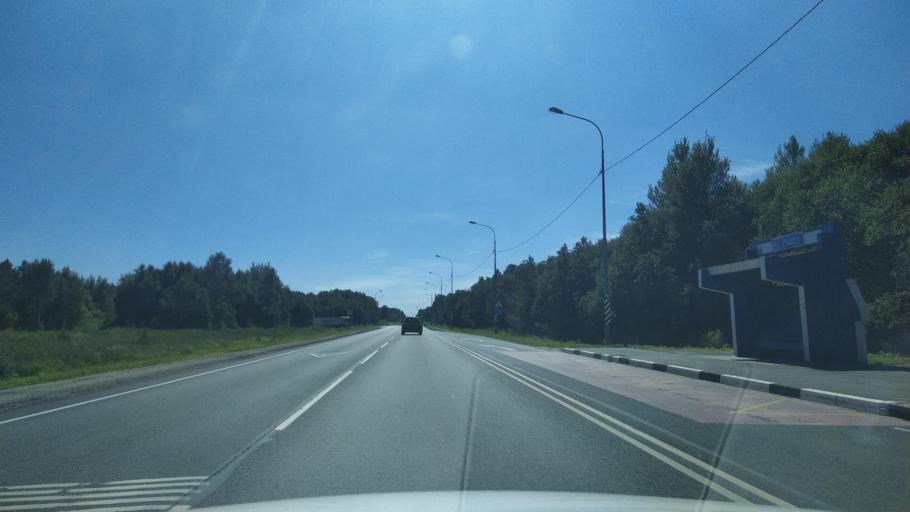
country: RU
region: Pskov
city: Pskov
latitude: 57.7851
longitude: 28.4079
